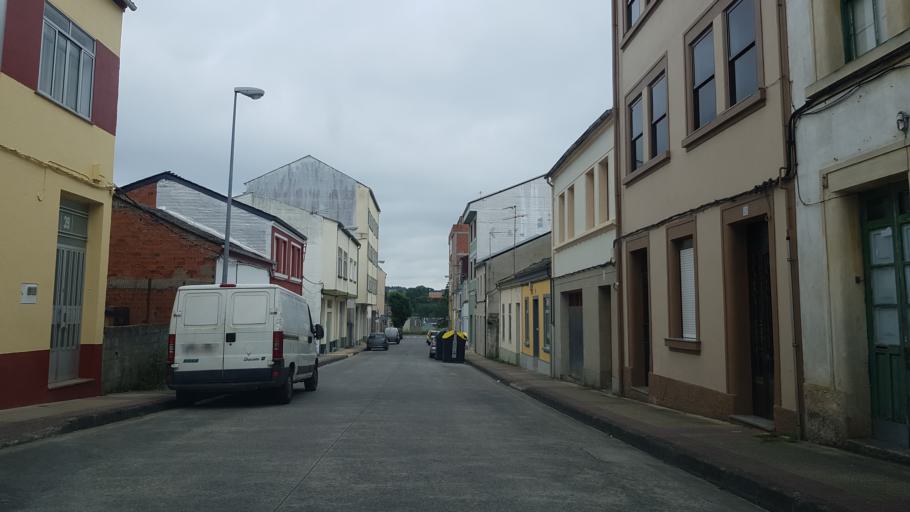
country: ES
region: Galicia
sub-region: Provincia de Lugo
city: Lugo
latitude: 43.0059
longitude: -7.5686
